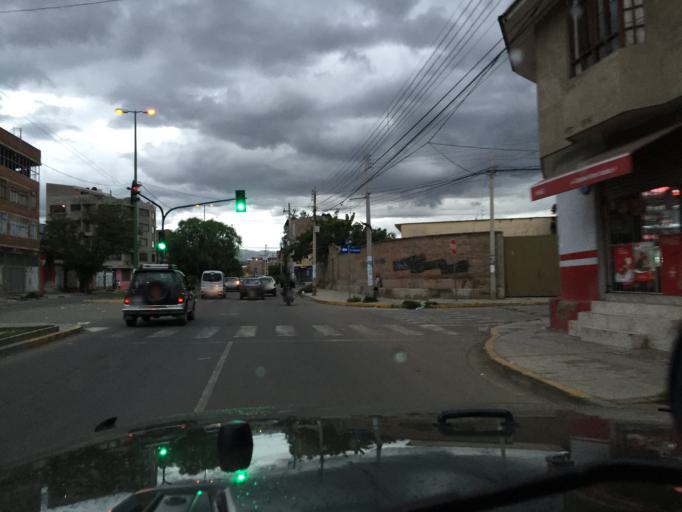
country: BO
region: Cochabamba
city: Cochabamba
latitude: -17.3966
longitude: -66.1878
